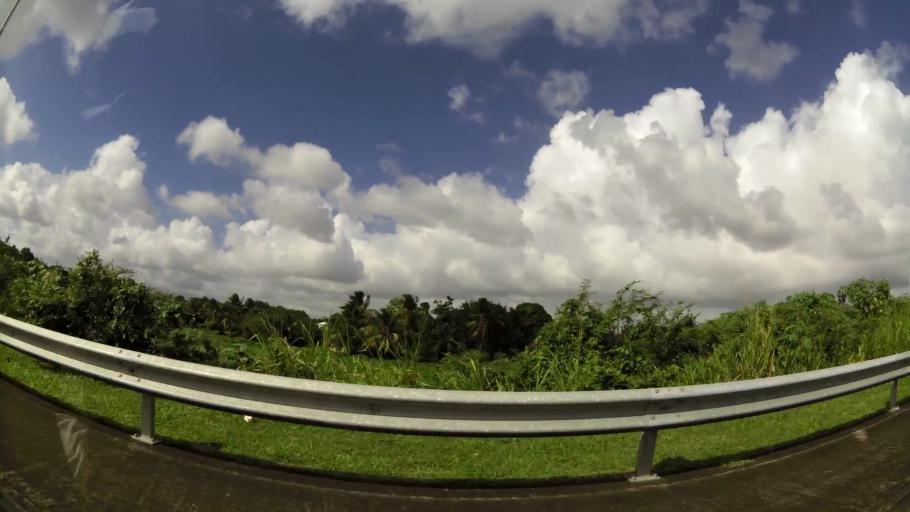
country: MQ
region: Martinique
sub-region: Martinique
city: Le Lamentin
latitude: 14.6196
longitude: -60.9951
